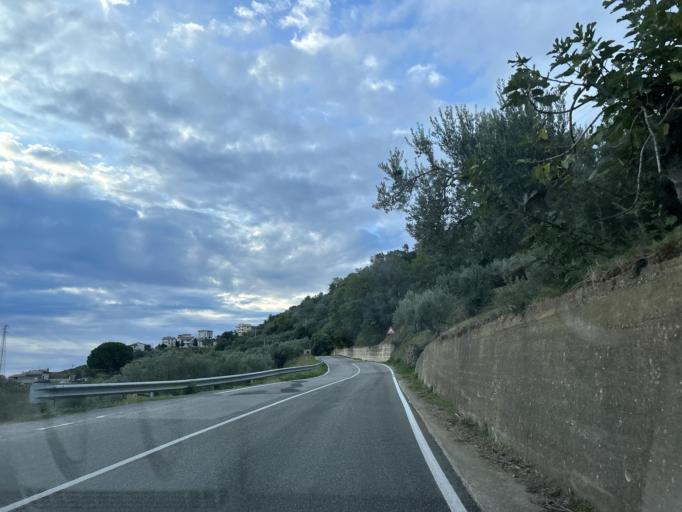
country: IT
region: Calabria
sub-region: Provincia di Catanzaro
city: Montauro
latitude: 38.7533
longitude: 16.5069
